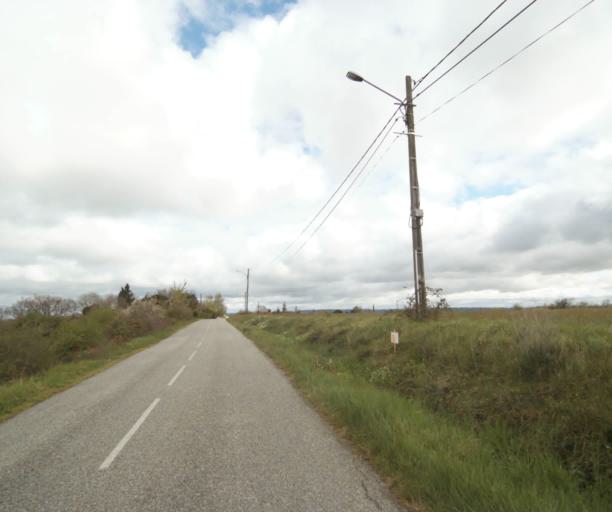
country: FR
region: Midi-Pyrenees
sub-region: Departement de l'Ariege
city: Saverdun
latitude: 43.2307
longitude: 1.5659
